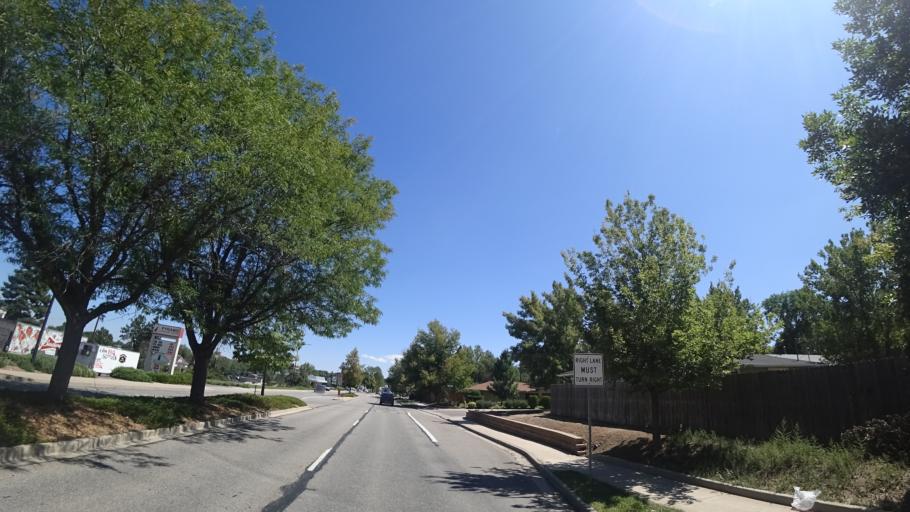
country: US
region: Colorado
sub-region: Arapahoe County
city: Littleton
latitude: 39.6132
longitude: -104.9949
